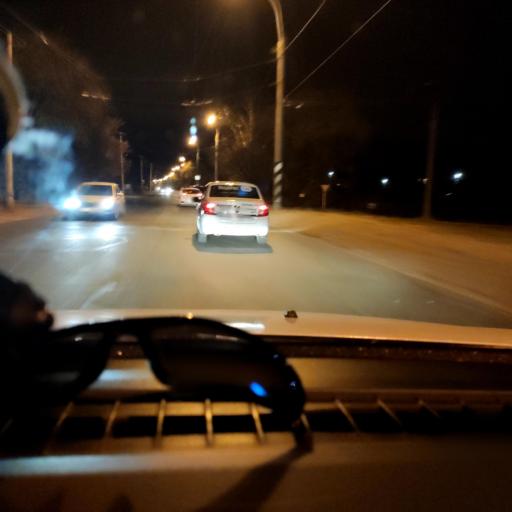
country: RU
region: Samara
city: Samara
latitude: 53.1486
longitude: 50.0945
